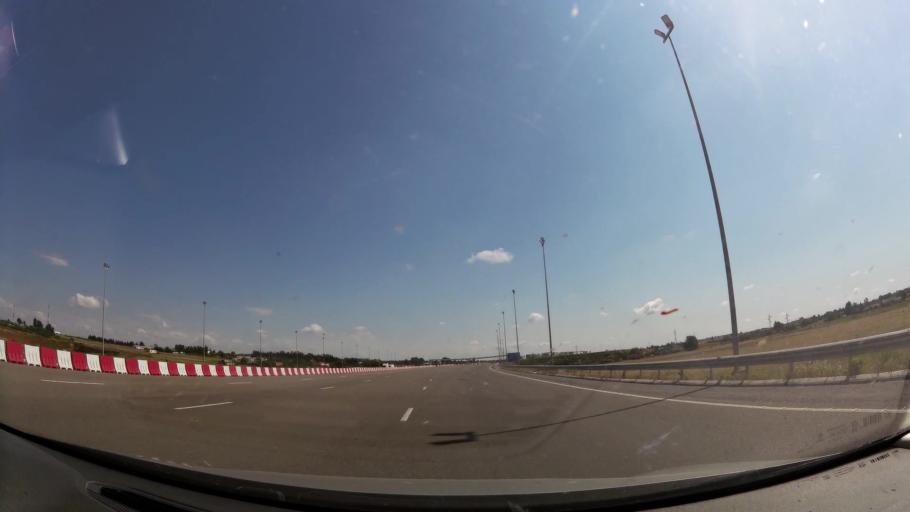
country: MA
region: Rabat-Sale-Zemmour-Zaer
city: Sale
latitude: 33.9692
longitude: -6.7401
